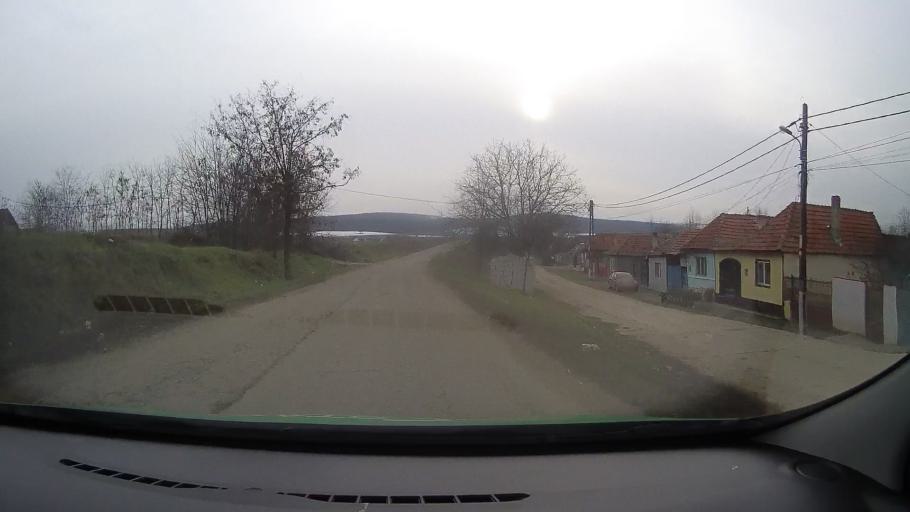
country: RO
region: Hunedoara
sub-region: Comuna Turdas
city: Turdas
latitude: 45.8460
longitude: 23.1218
